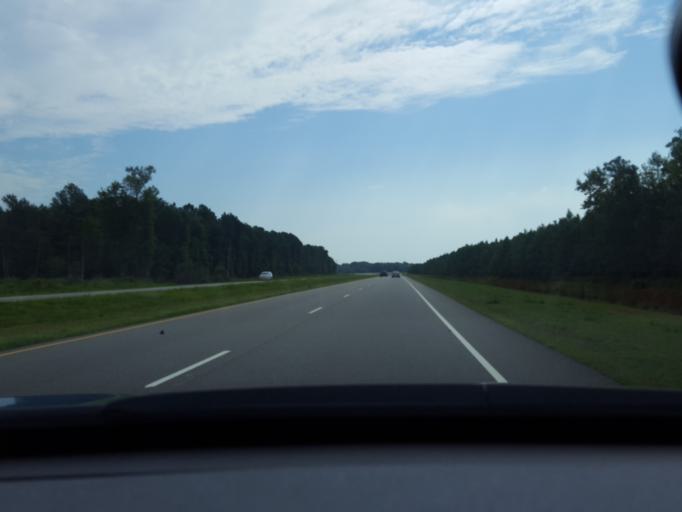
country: US
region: North Carolina
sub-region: Chowan County
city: Edenton
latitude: 36.0371
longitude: -76.7323
